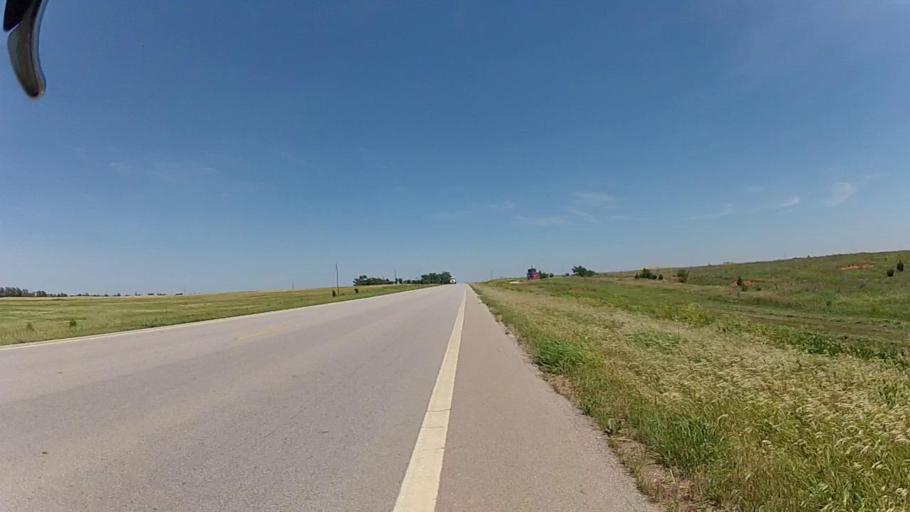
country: US
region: Kansas
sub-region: Harper County
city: Harper
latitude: 37.2386
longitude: -98.1158
